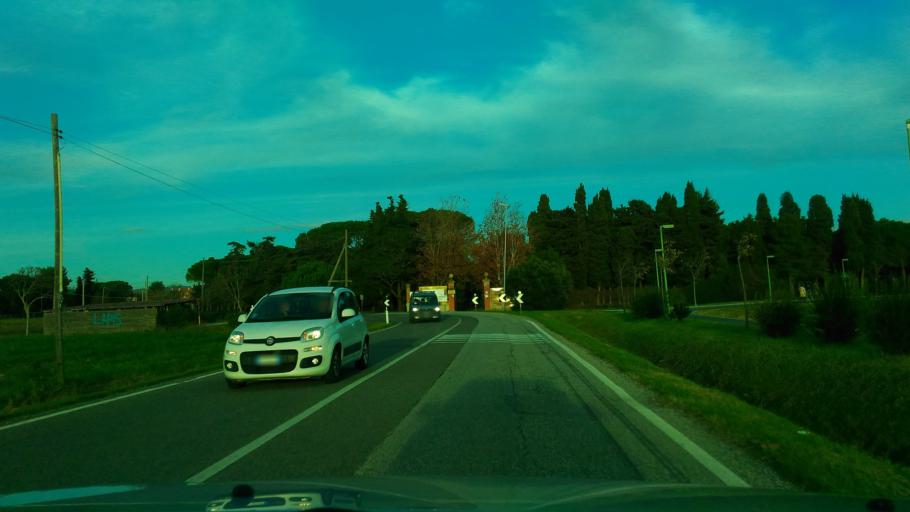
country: IT
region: Tuscany
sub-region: Provincia di Livorno
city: S.P. in Palazzi
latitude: 43.3172
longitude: 10.4965
